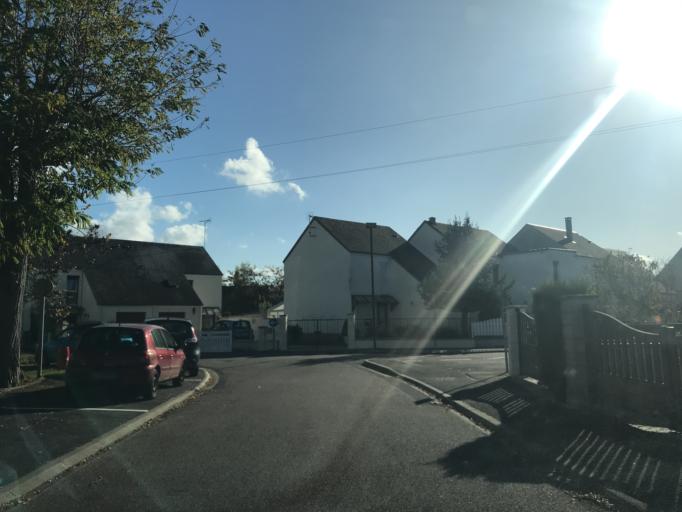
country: FR
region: Haute-Normandie
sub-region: Departement de l'Eure
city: Saint-Marcel
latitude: 49.1017
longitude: 1.4478
